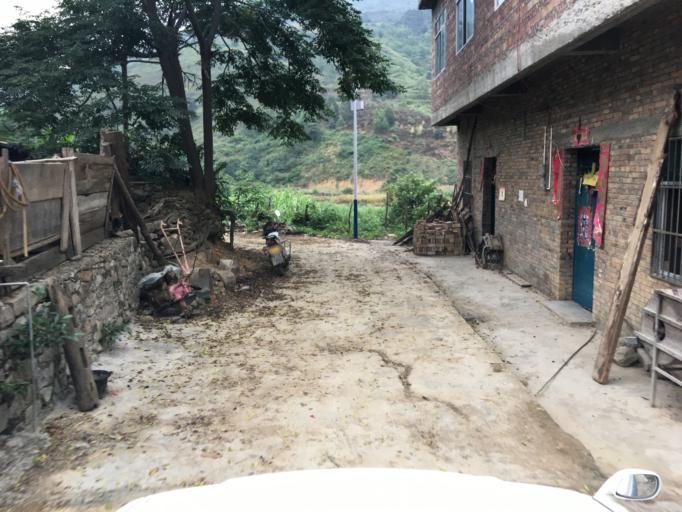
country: CN
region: Guangxi Zhuangzu Zizhiqu
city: Leli
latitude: 24.7684
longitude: 106.0923
